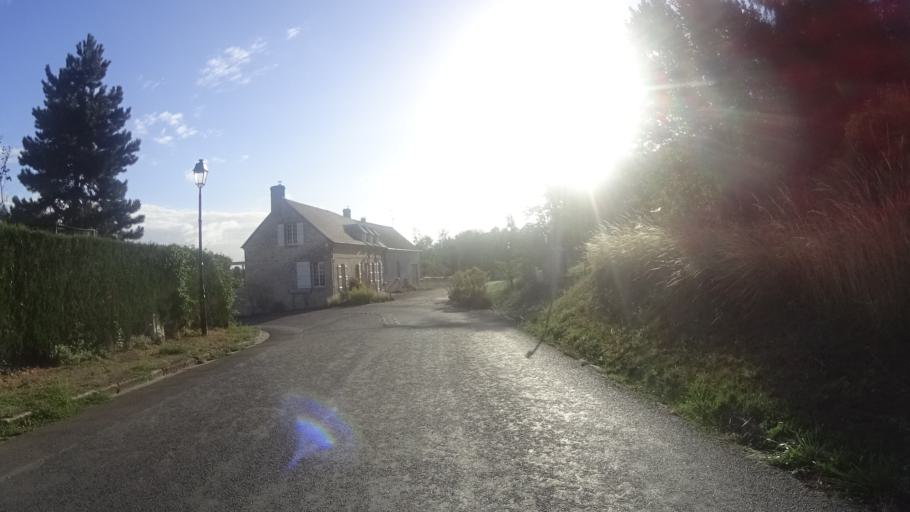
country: FR
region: Picardie
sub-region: Departement de l'Oise
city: Verberie
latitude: 49.3074
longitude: 2.6994
